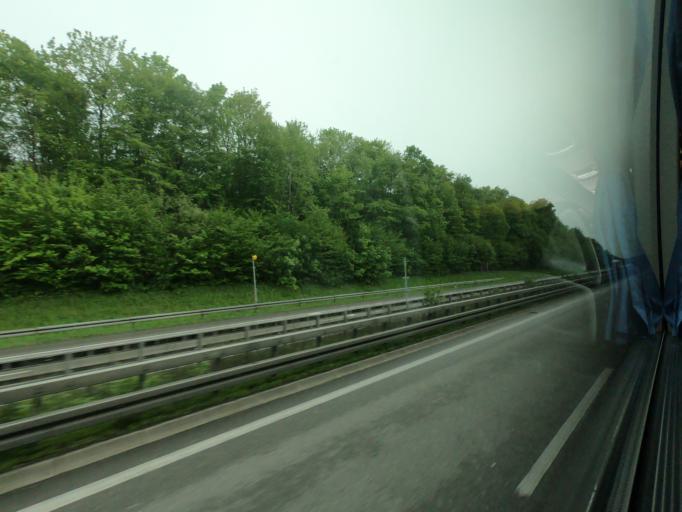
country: DE
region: Baden-Wuerttemberg
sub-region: Regierungsbezirk Stuttgart
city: Bretzfeld
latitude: 49.1770
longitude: 9.4043
